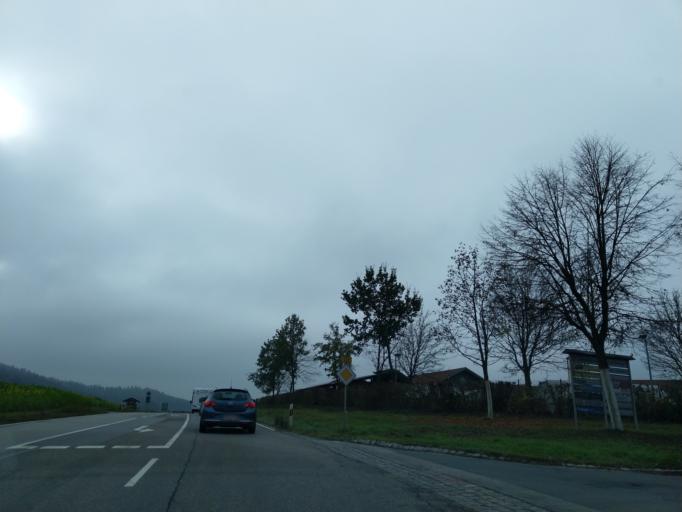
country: DE
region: Bavaria
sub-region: Lower Bavaria
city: Auerbach
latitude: 48.8025
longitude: 13.0930
